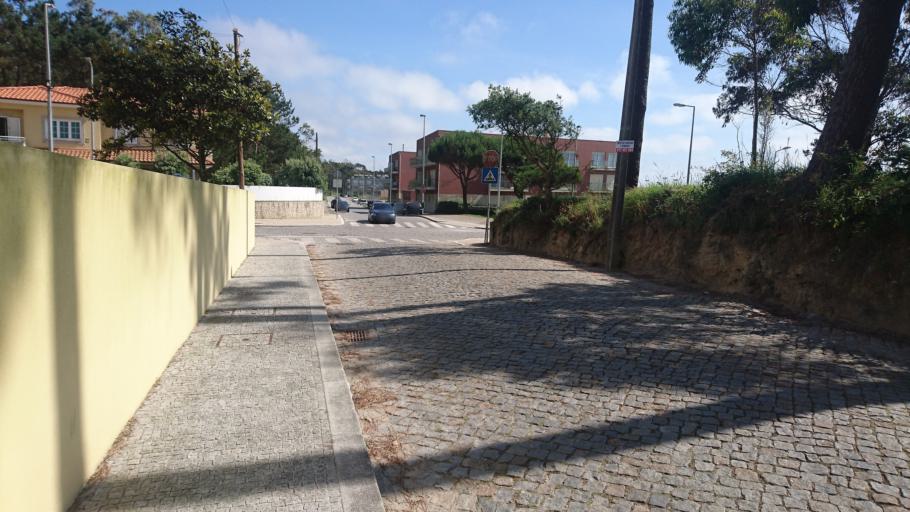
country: PT
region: Porto
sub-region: Matosinhos
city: Lavra
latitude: 41.2766
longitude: -8.7235
